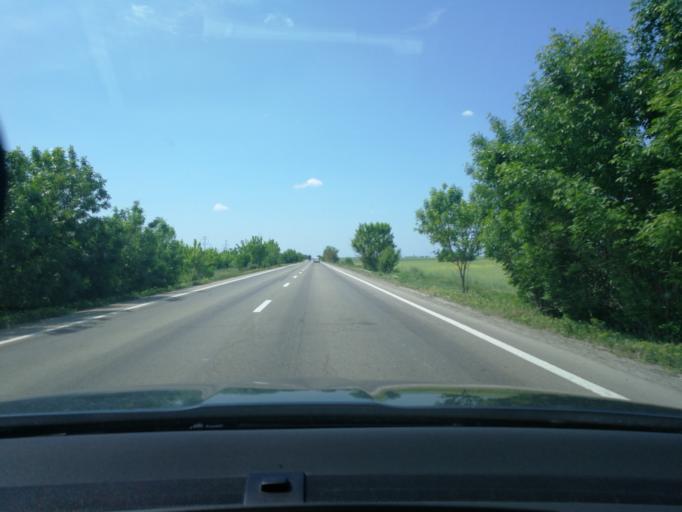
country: RO
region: Prahova
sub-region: Comuna Targsoru Vechi
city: Strejnicu
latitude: 44.8902
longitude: 25.9588
